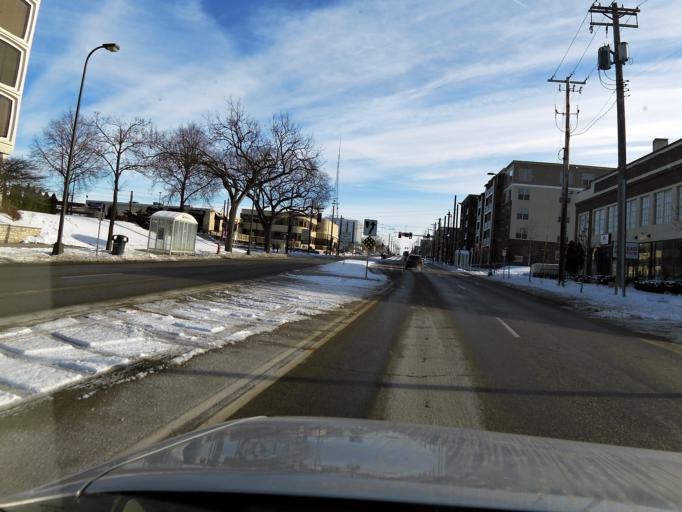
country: US
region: Minnesota
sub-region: Ramsey County
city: Lauderdale
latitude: 44.9714
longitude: -93.2164
